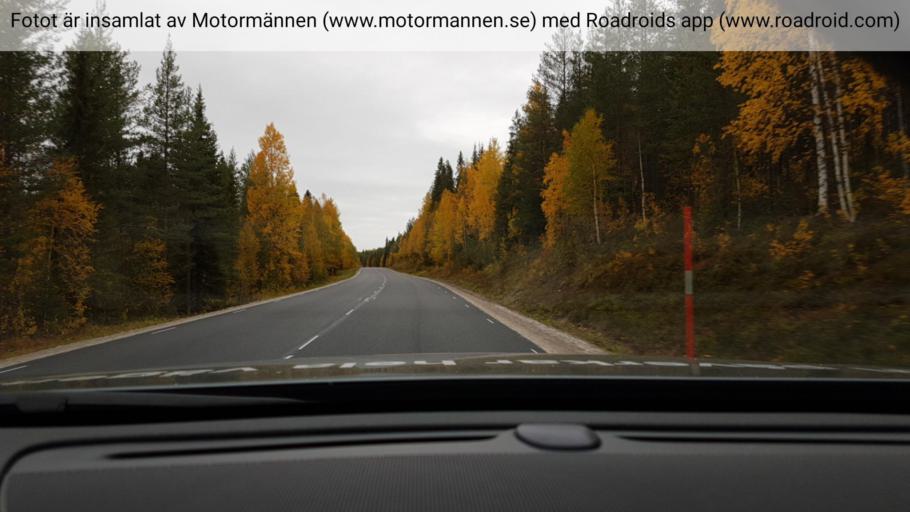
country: SE
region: Norrbotten
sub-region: Overkalix Kommun
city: OEverkalix
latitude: 66.4628
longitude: 22.7929
